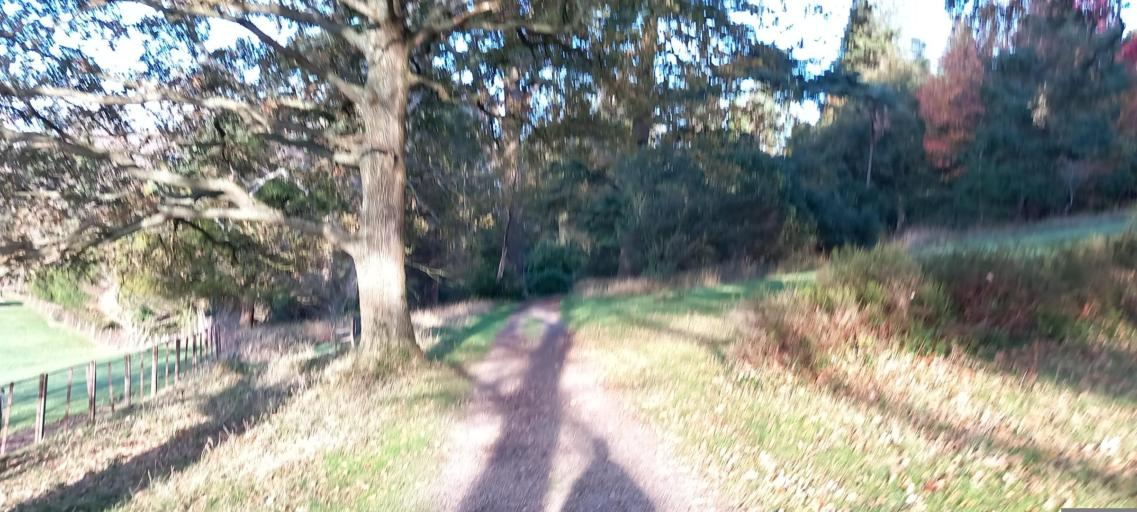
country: GB
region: Wales
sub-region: Gwynedd
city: Bangor
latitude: 53.2243
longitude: -4.0964
